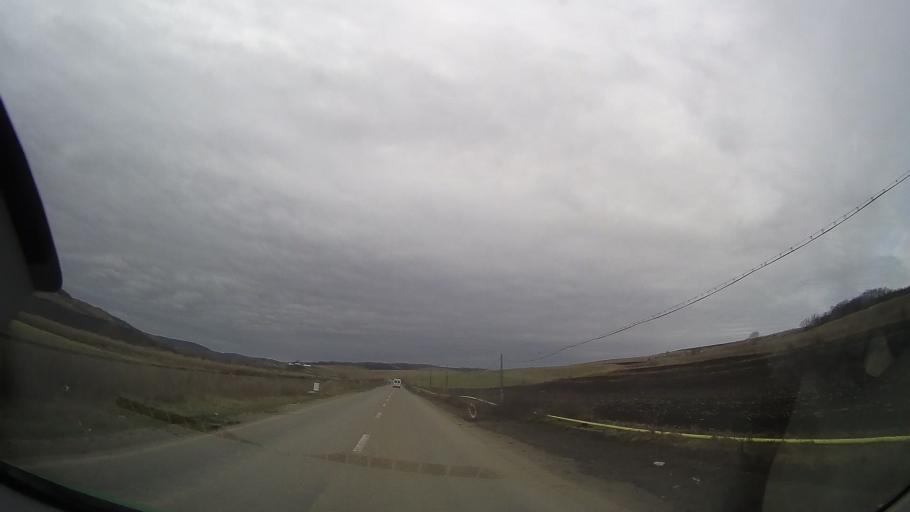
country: RO
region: Cluj
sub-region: Comuna Catina
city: Catina
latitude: 46.8101
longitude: 24.2210
